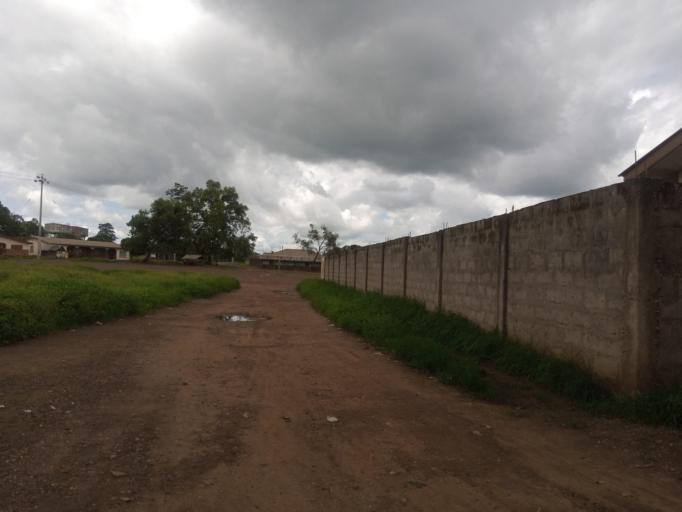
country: SL
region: Northern Province
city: Port Loko
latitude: 8.7648
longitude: -12.7799
